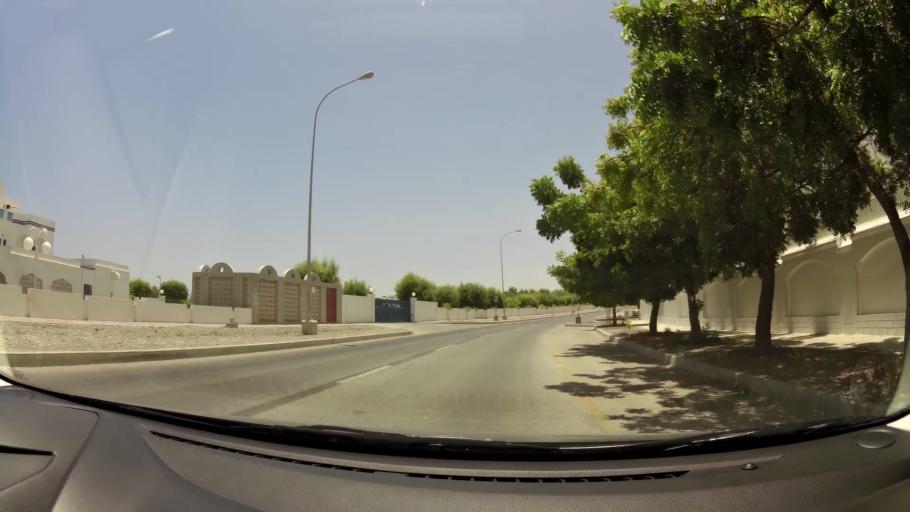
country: OM
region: Muhafazat Masqat
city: Bawshar
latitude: 23.6140
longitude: 58.4600
